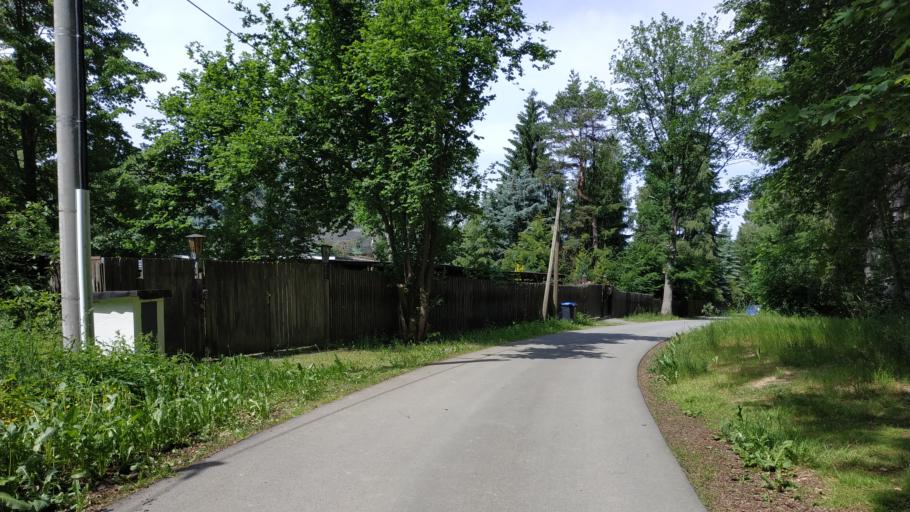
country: DE
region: Saxony
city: Plauen
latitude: 50.5330
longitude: 12.1196
